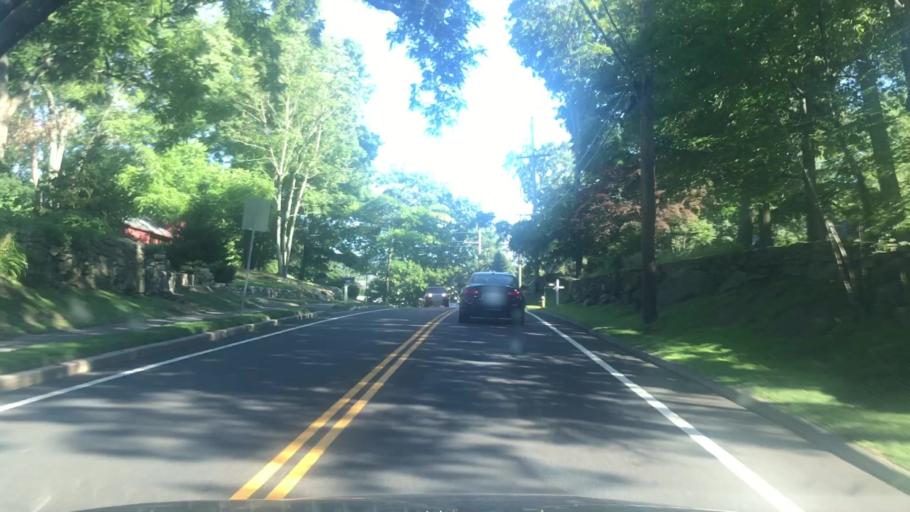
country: US
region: Connecticut
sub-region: Fairfield County
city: Glenville
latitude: 41.0322
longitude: -73.6572
